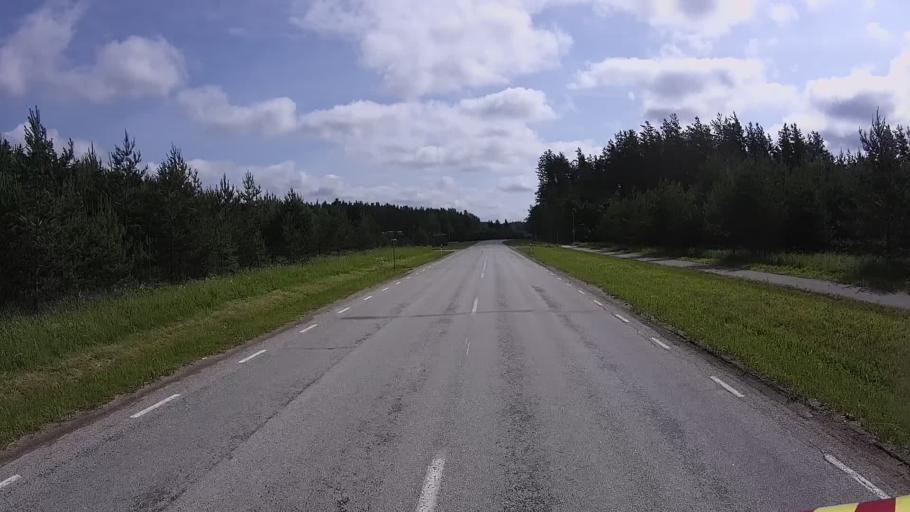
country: EE
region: Vorumaa
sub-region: Voru linn
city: Voru
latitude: 57.8511
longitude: 26.8581
